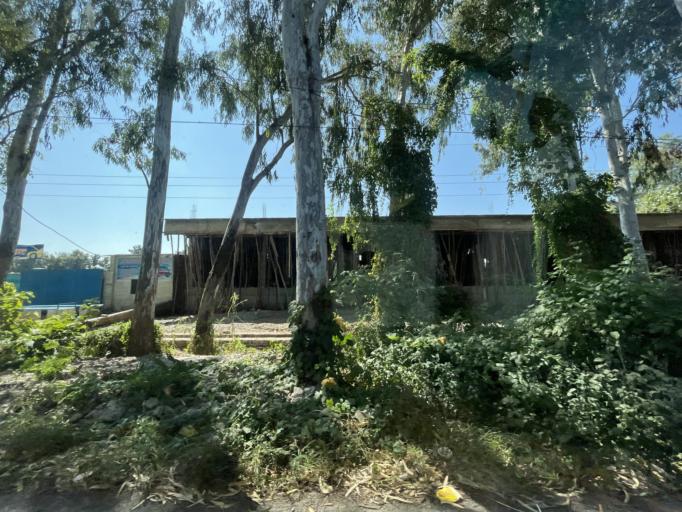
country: IN
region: Uttarakhand
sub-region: Naini Tal
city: Haldwani
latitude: 29.2126
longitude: 79.4577
